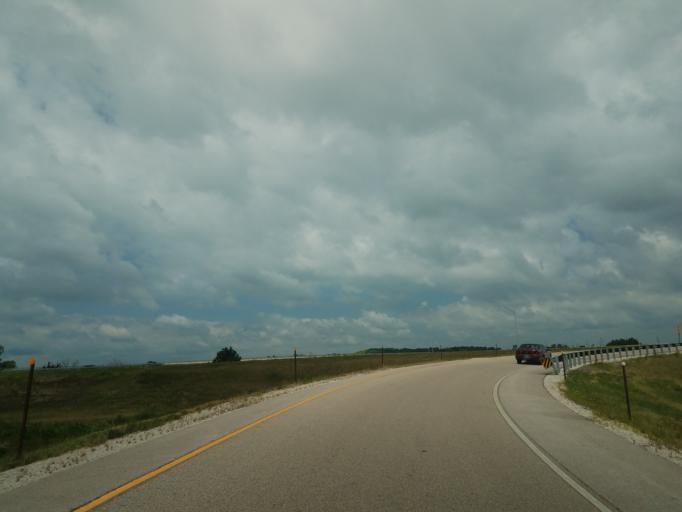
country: US
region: Illinois
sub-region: McLean County
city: Bloomington
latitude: 40.4389
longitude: -89.0201
